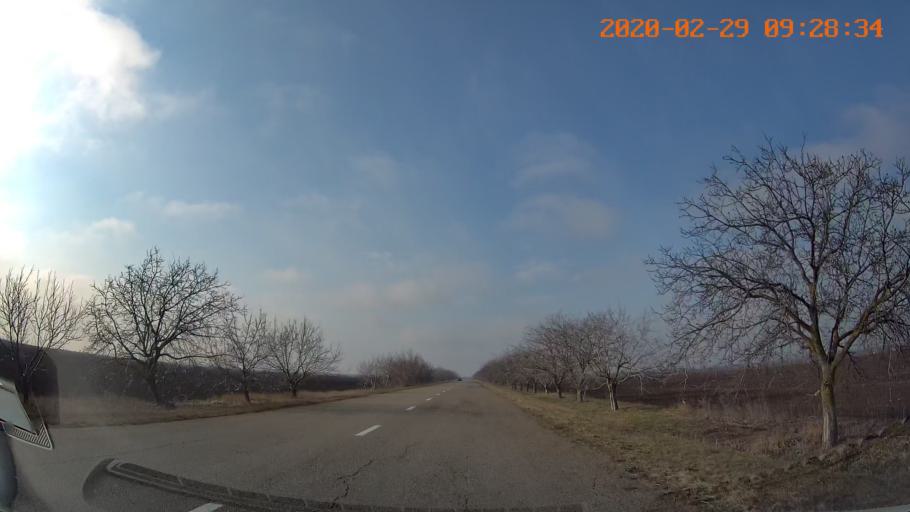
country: UA
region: Odessa
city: Lymanske
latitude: 46.6875
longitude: 29.9284
